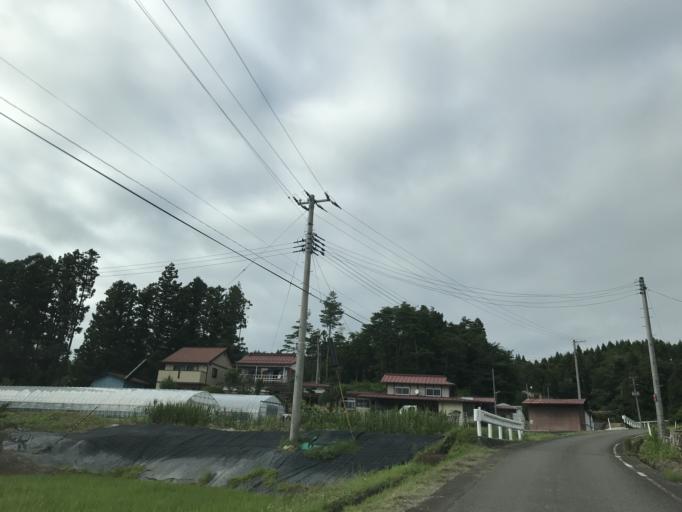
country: JP
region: Iwate
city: Ichinoseki
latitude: 38.8249
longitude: 141.2076
